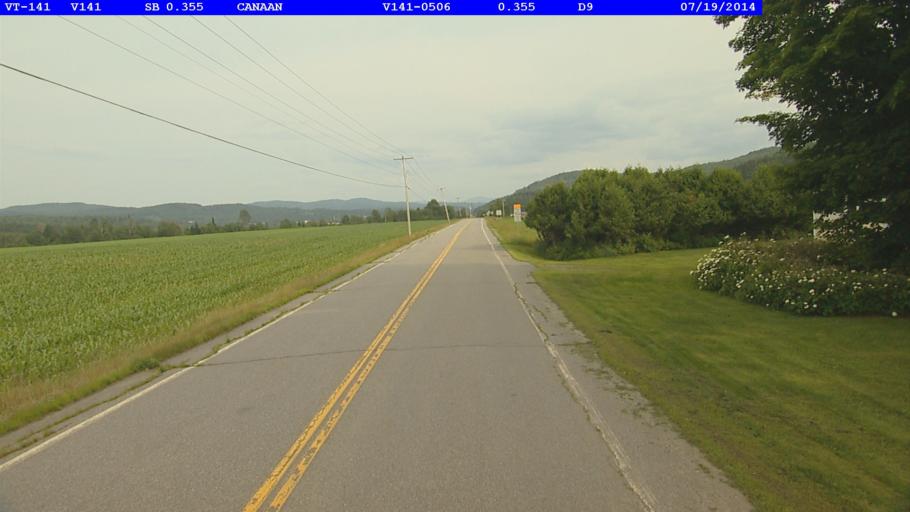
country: US
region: New Hampshire
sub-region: Coos County
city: Colebrook
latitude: 45.0111
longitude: -71.5590
